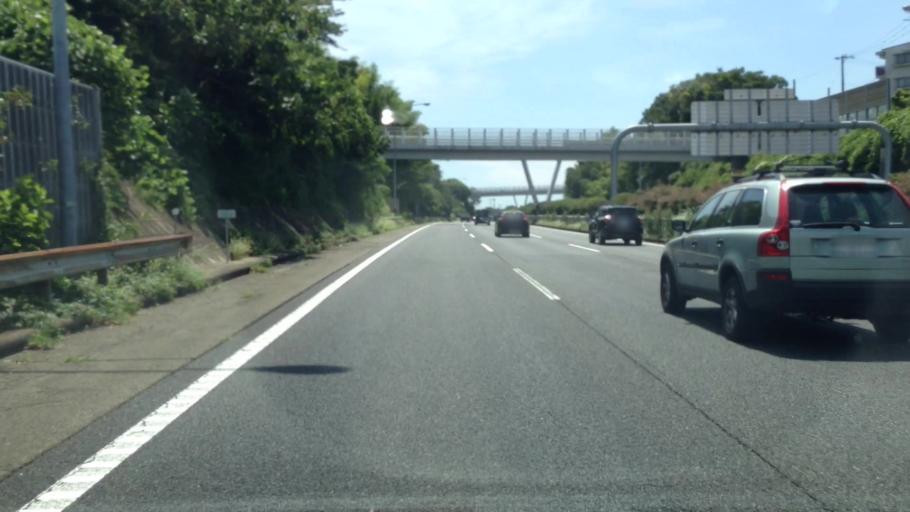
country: JP
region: Kanagawa
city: Yokohama
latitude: 35.5074
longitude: 139.5931
